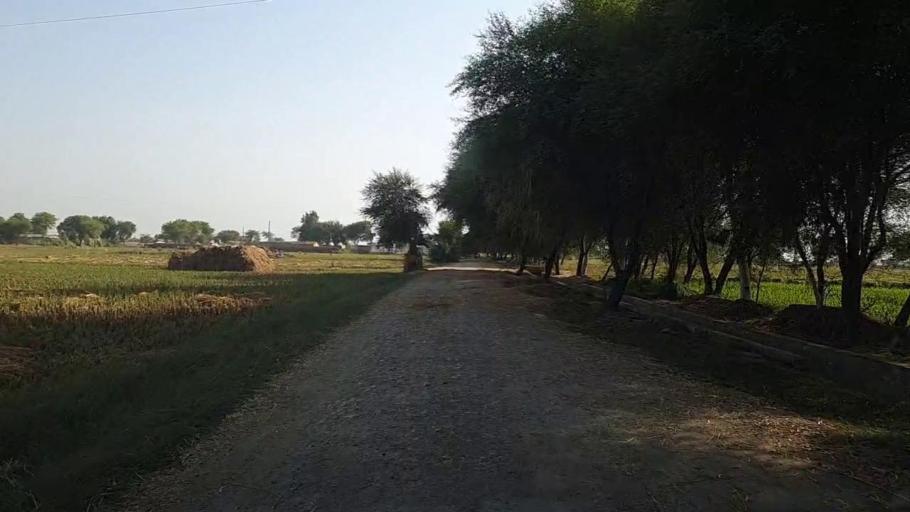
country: PK
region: Sindh
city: Kandhkot
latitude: 28.3531
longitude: 69.3351
